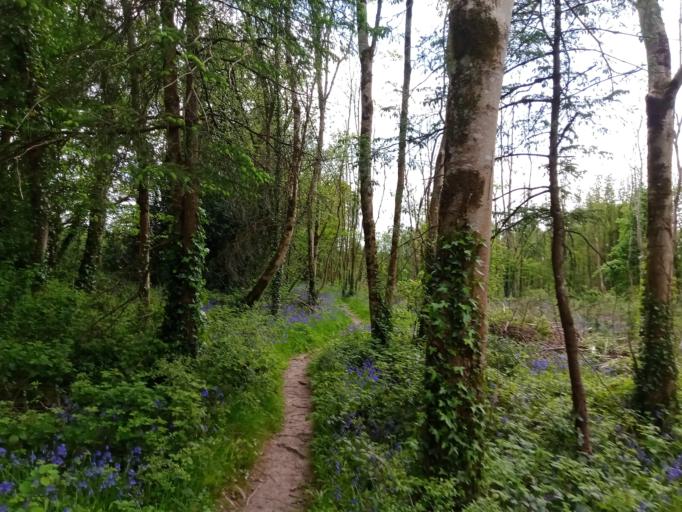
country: IE
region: Leinster
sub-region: Kilkenny
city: Castlecomer
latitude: 52.8210
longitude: -7.2024
